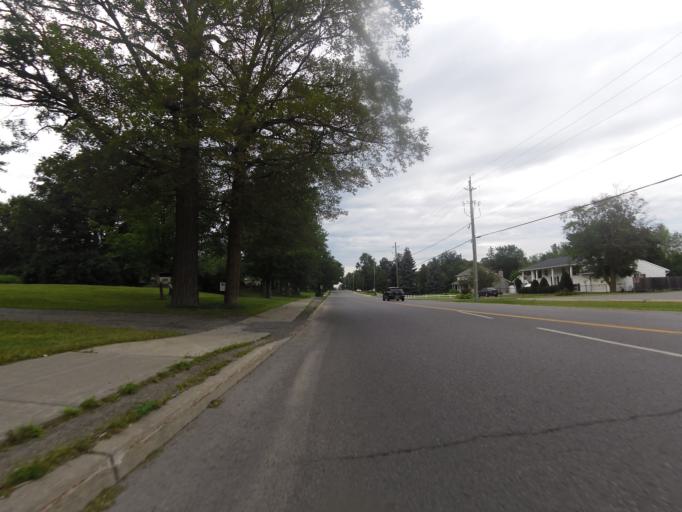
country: CA
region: Ontario
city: Carleton Place
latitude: 45.1303
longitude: -76.1295
